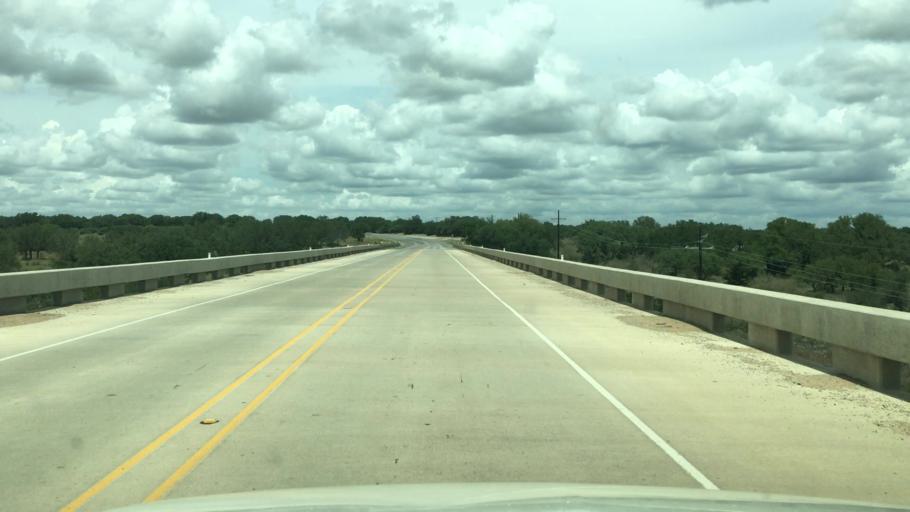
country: US
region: Texas
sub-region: McCulloch County
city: Brady
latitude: 31.0145
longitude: -99.2097
